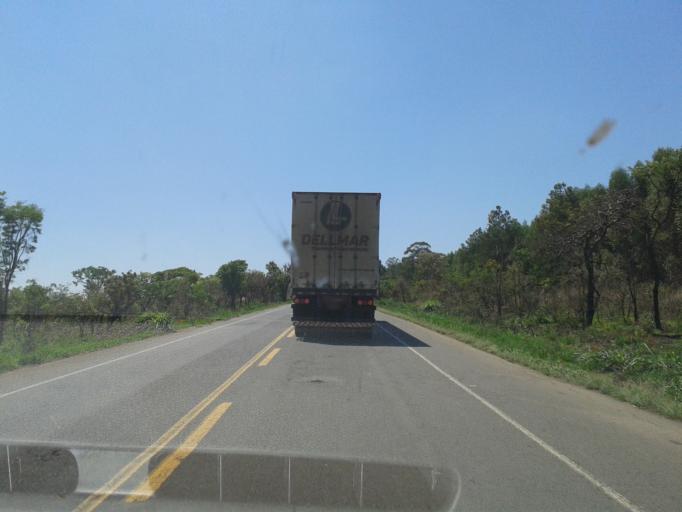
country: BR
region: Minas Gerais
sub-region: Araxa
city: Araxa
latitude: -19.4361
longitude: -47.2083
